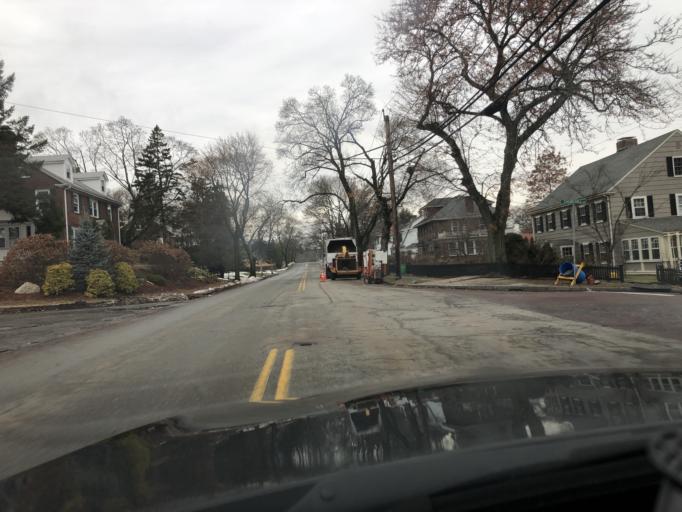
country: US
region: Massachusetts
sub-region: Middlesex County
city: Arlington
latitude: 42.4130
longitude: -71.1642
